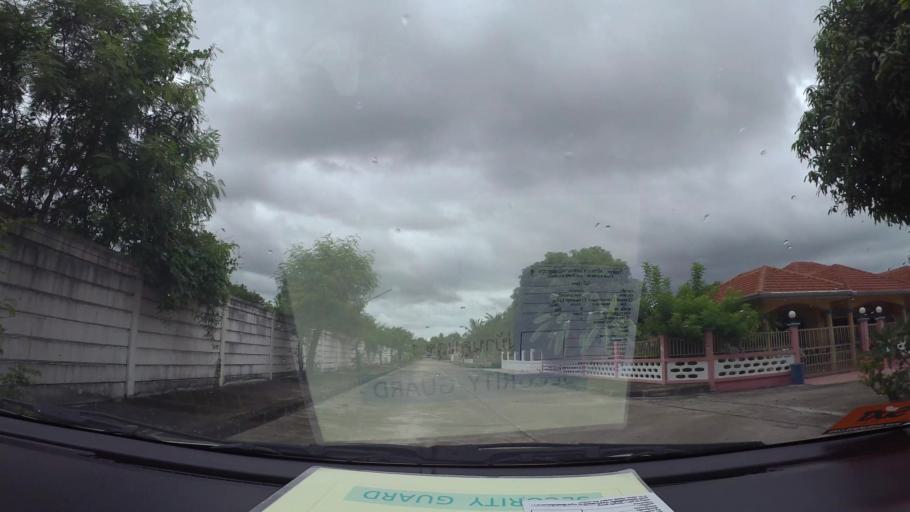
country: TH
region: Chon Buri
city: Sattahip
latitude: 12.7611
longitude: 100.9097
